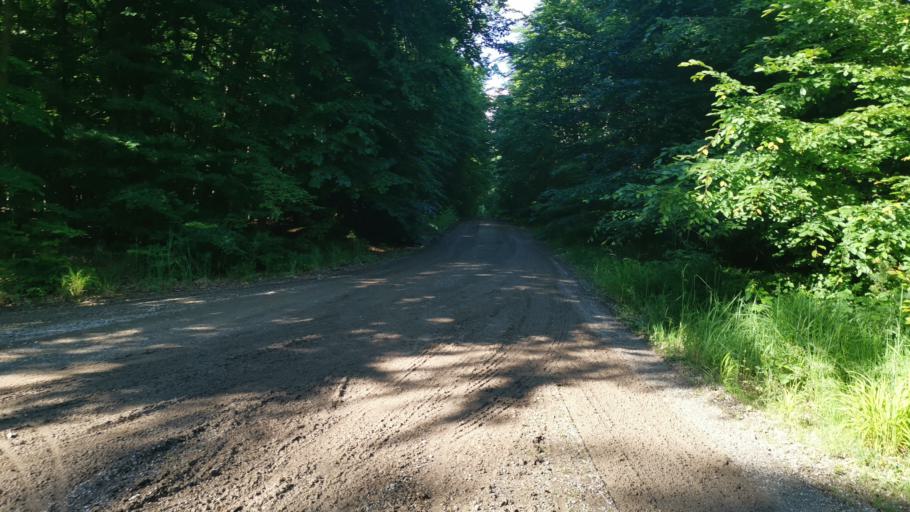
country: DE
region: Bavaria
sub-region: Lower Bavaria
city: Aiglsbach
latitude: 48.7276
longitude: 11.7589
